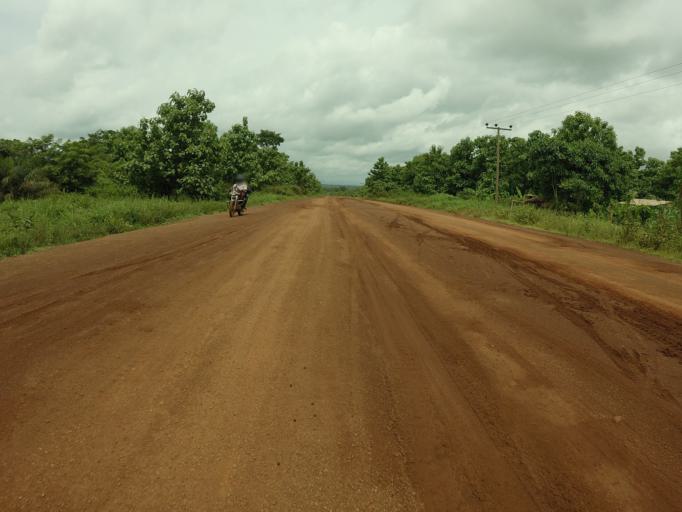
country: GH
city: Kpandae
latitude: 8.4110
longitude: 0.3940
